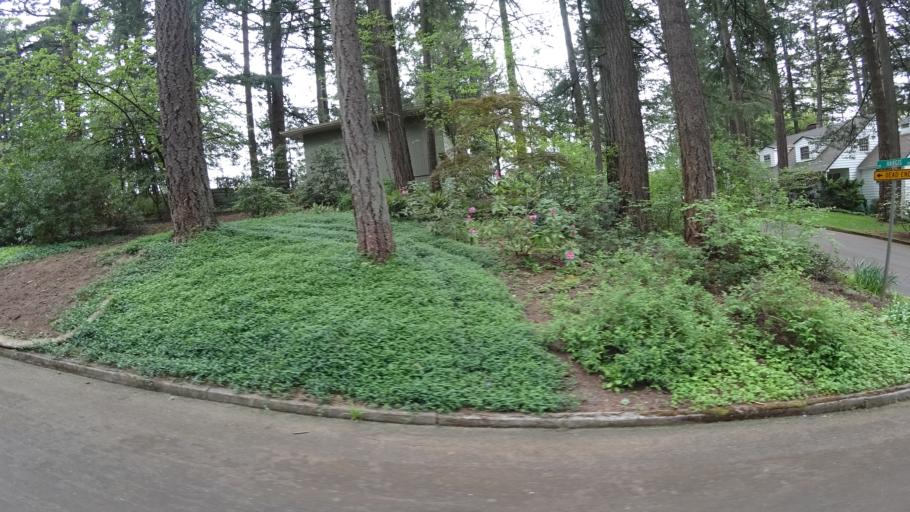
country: US
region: Oregon
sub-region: Washington County
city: Beaverton
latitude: 45.4625
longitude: -122.8171
